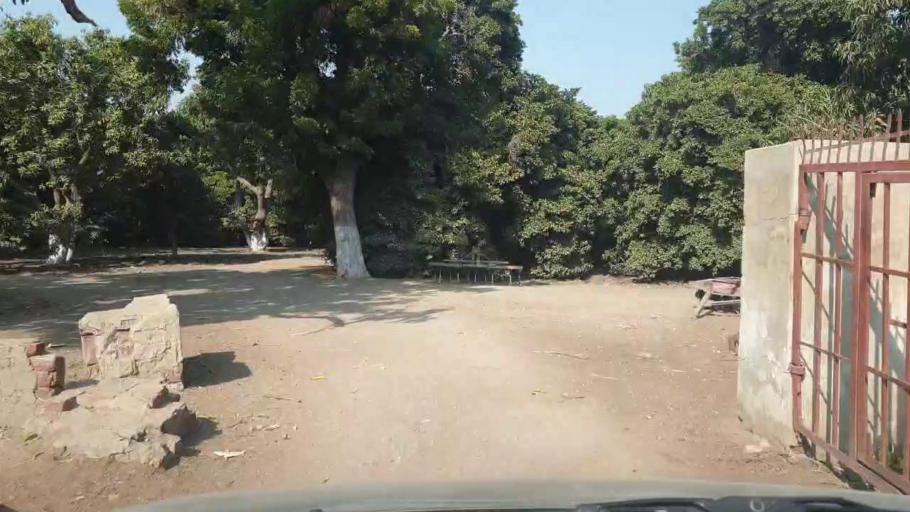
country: PK
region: Sindh
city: Digri
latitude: 25.2565
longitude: 69.1482
